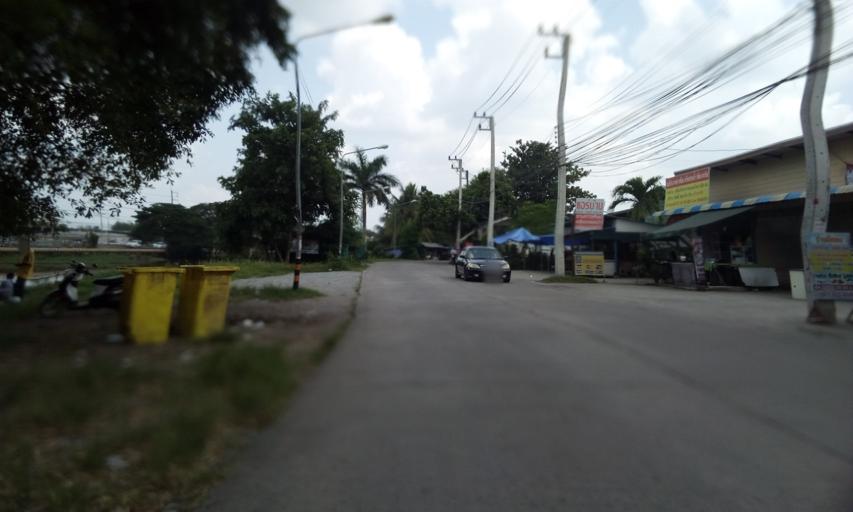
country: TH
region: Pathum Thani
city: Ban Rangsit
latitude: 14.0346
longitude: 100.7736
